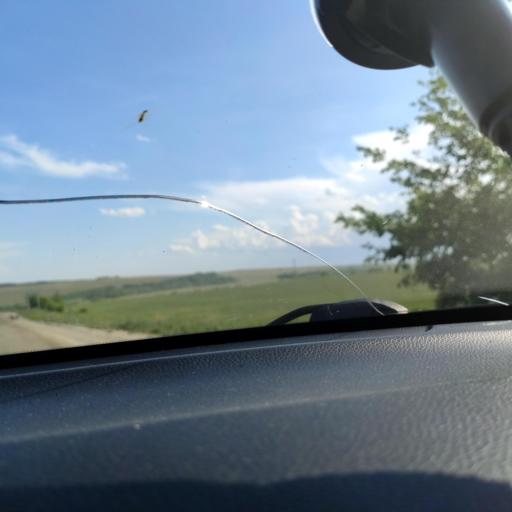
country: RU
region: Tatarstan
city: Verkhniy Uslon
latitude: 55.6481
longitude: 48.9390
